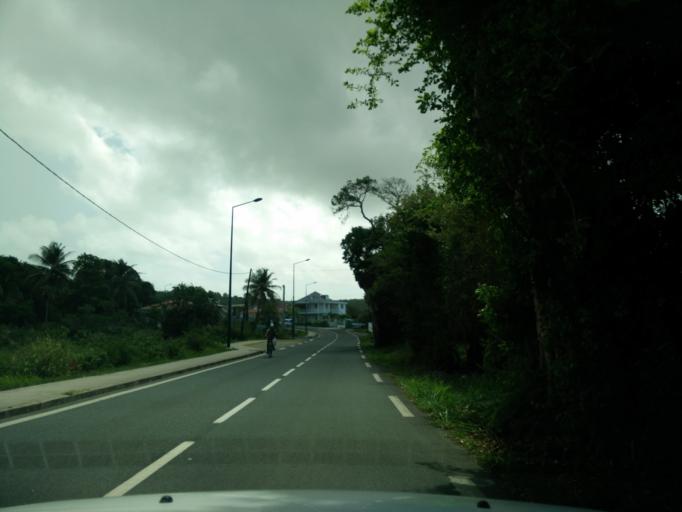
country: GP
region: Guadeloupe
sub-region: Guadeloupe
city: Grand-Bourg
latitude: 15.8837
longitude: -61.3070
